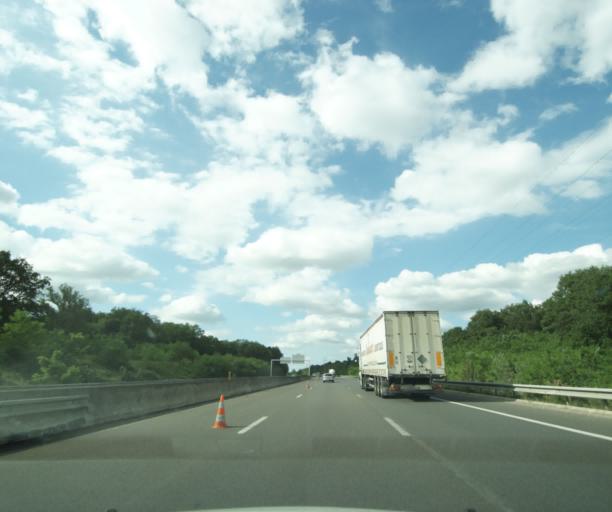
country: FR
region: Centre
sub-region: Departement du Loiret
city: Saint-Pryve-Saint-Mesmin
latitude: 47.8476
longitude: 1.8666
